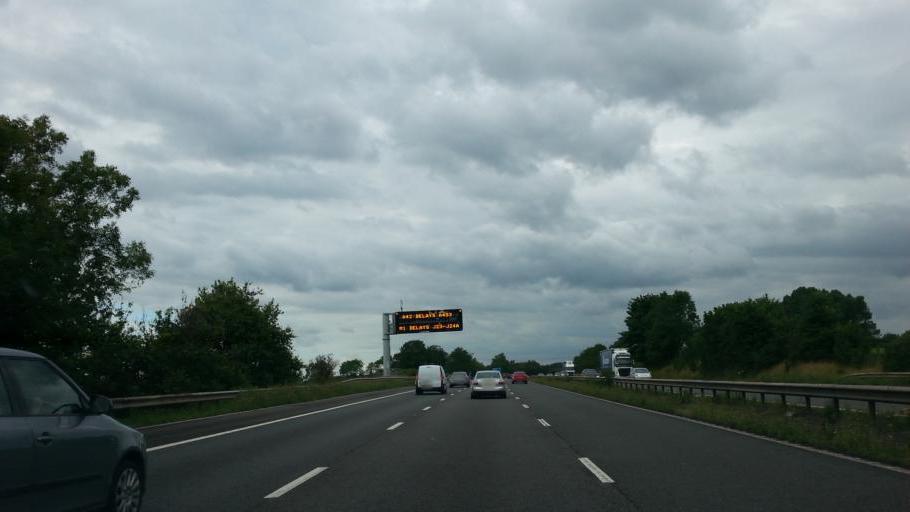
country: GB
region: England
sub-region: Leicestershire
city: Hinckley
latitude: 52.4988
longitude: -1.3835
